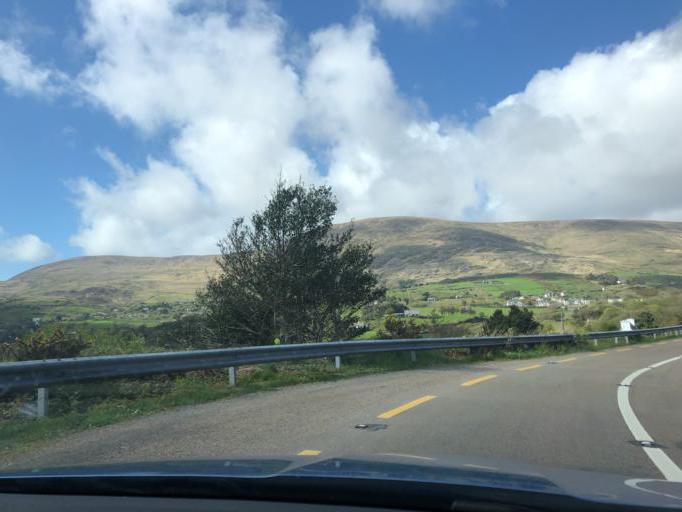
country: IE
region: Munster
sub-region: Ciarrai
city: Cahersiveen
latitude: 51.7636
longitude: -10.0999
